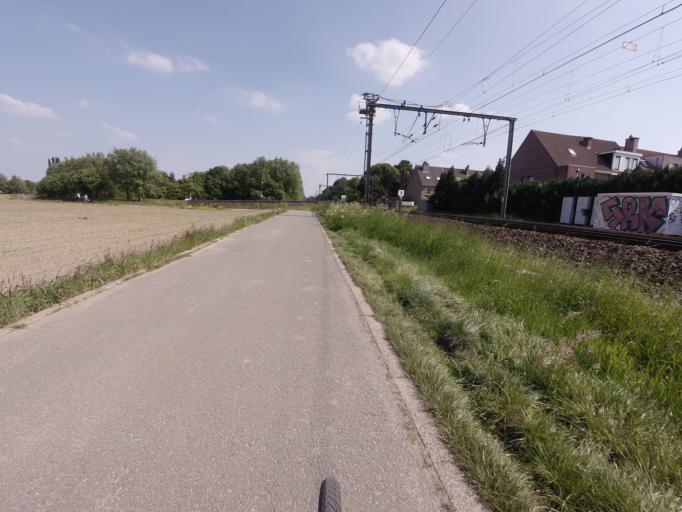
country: BE
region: Flanders
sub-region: Provincie Antwerpen
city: Boechout
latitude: 51.1728
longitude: 4.4786
